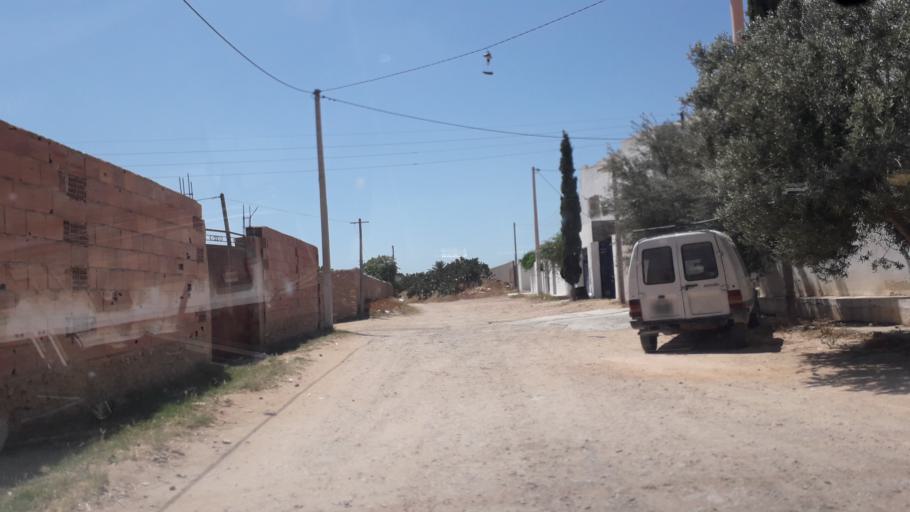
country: TN
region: Safaqis
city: Al Qarmadah
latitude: 34.8224
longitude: 10.7691
